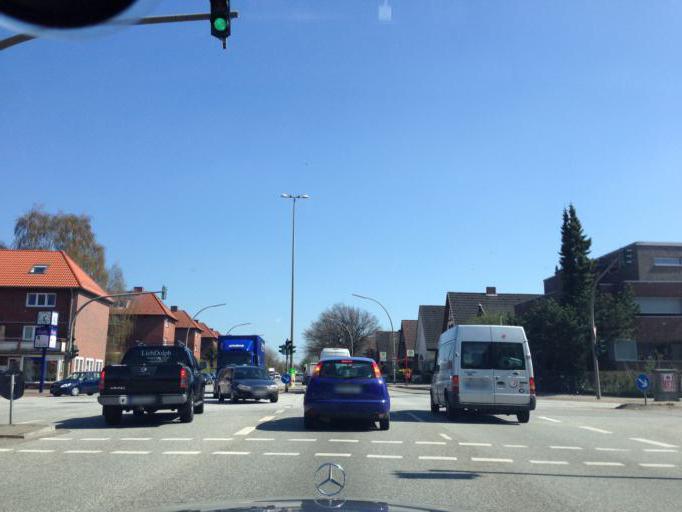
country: DE
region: Hamburg
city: Steilshoop
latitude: 53.6085
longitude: 10.0670
